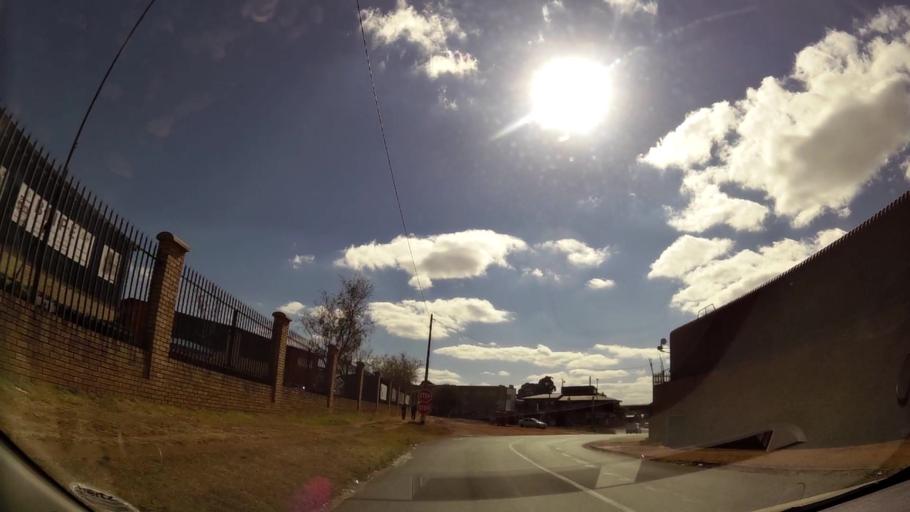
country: ZA
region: Gauteng
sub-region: West Rand District Municipality
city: Krugersdorp
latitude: -26.1162
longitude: 27.8149
